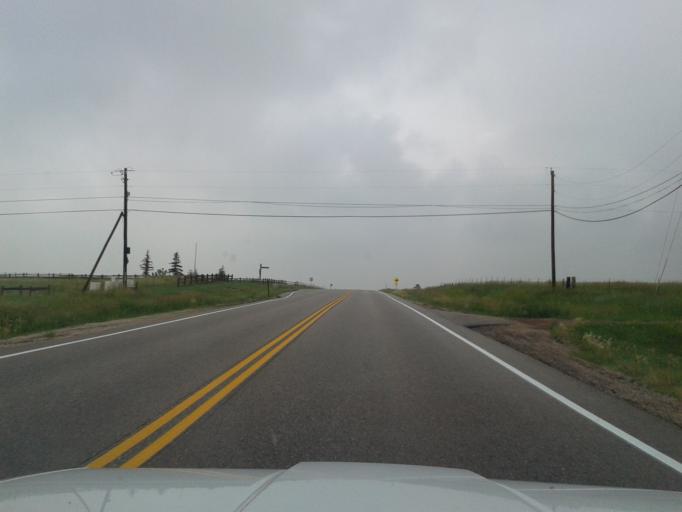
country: US
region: Colorado
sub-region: Elbert County
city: Ponderosa Park
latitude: 39.3402
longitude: -104.7338
